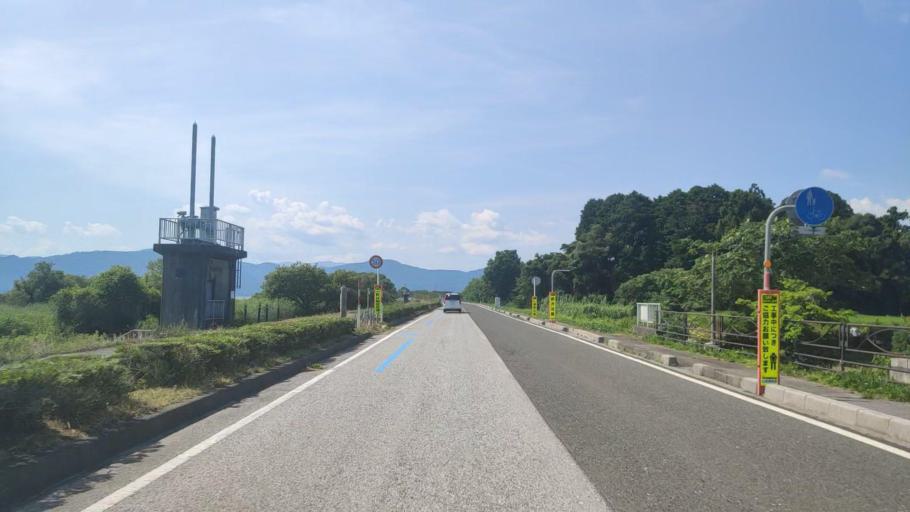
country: JP
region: Shiga Prefecture
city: Nagahama
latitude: 35.4354
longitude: 136.1954
